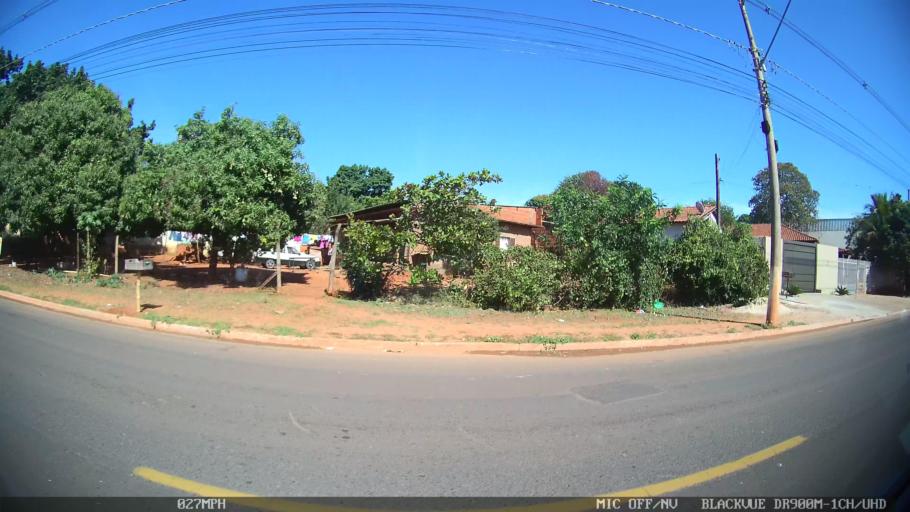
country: BR
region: Sao Paulo
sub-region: Sao Jose Do Rio Preto
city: Sao Jose do Rio Preto
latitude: -20.7603
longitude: -49.4333
